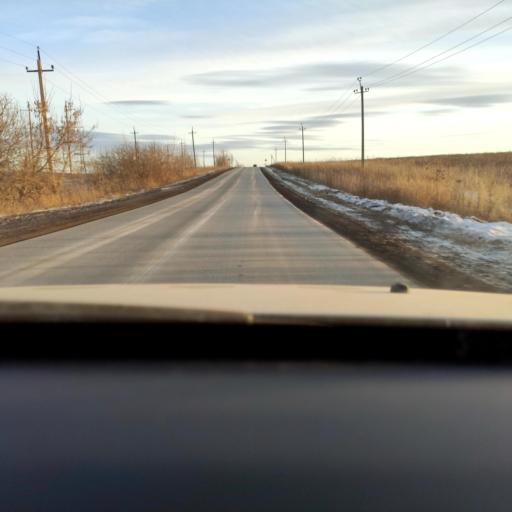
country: RU
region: Perm
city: Ferma
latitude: 57.9159
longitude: 56.3088
